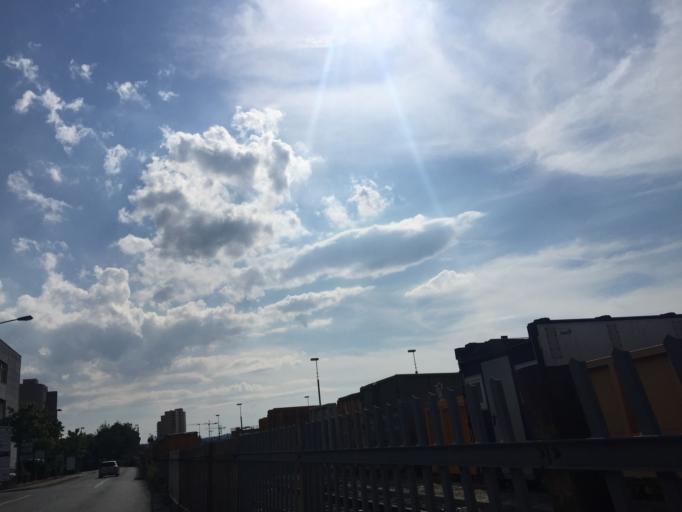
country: CH
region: Bern
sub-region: Bern-Mittelland District
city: Koniz
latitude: 46.9499
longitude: 7.4168
